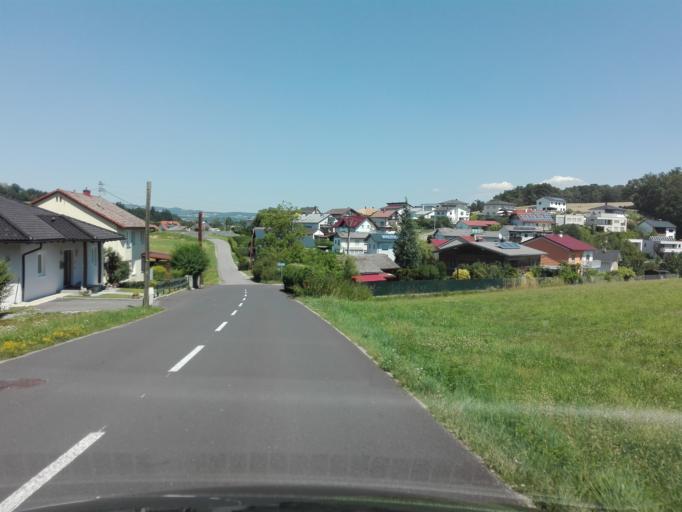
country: AT
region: Upper Austria
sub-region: Politischer Bezirk Urfahr-Umgebung
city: Gallneukirchen
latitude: 48.3314
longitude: 14.3852
